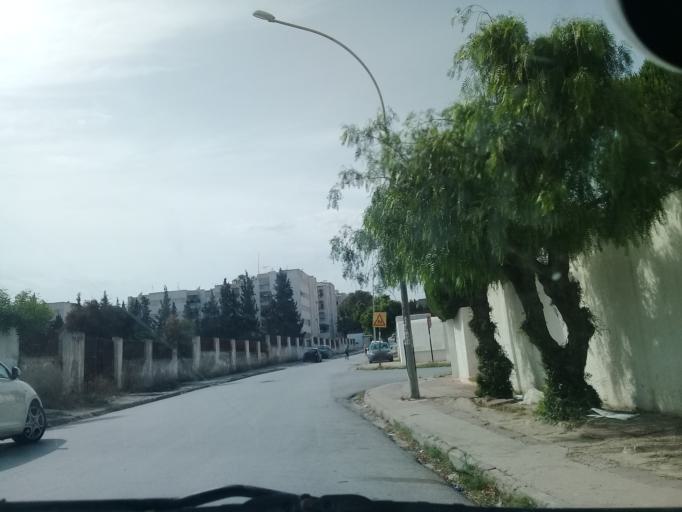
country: TN
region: Tunis
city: Tunis
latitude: 36.8487
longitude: 10.1593
